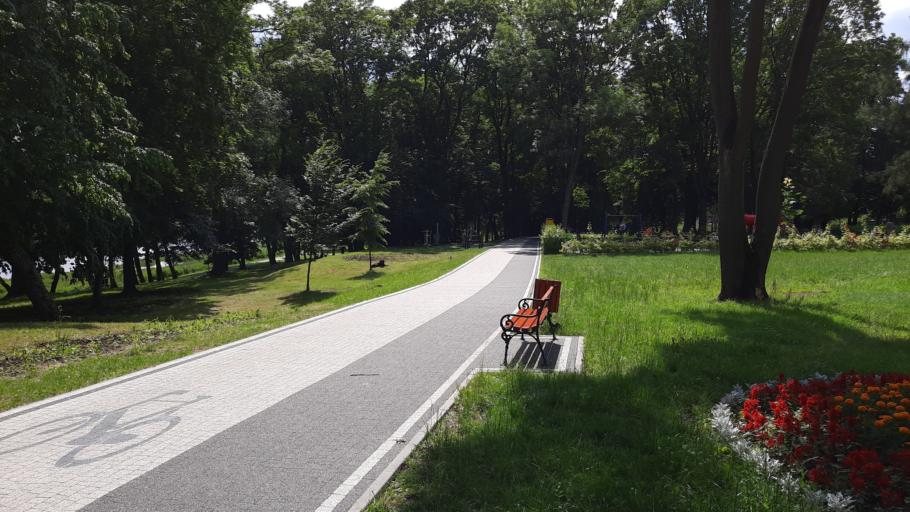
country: PL
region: Masovian Voivodeship
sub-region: Powiat wyszkowski
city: Wyszkow
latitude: 52.5905
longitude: 21.4554
